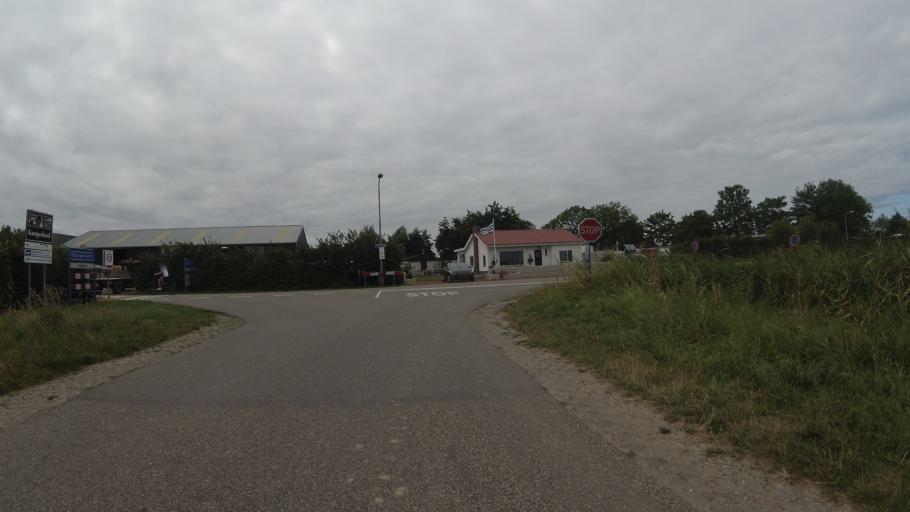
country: NL
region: Zeeland
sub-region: Gemeente Noord-Beveland
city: Kamperland
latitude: 51.5766
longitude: 3.7012
